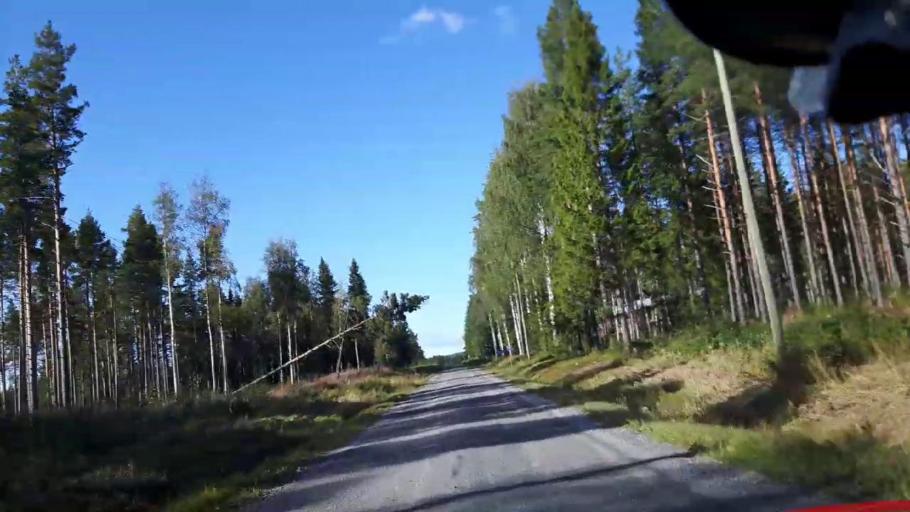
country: SE
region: Jaemtland
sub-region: Ragunda Kommun
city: Hammarstrand
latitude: 63.5191
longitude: 16.0564
